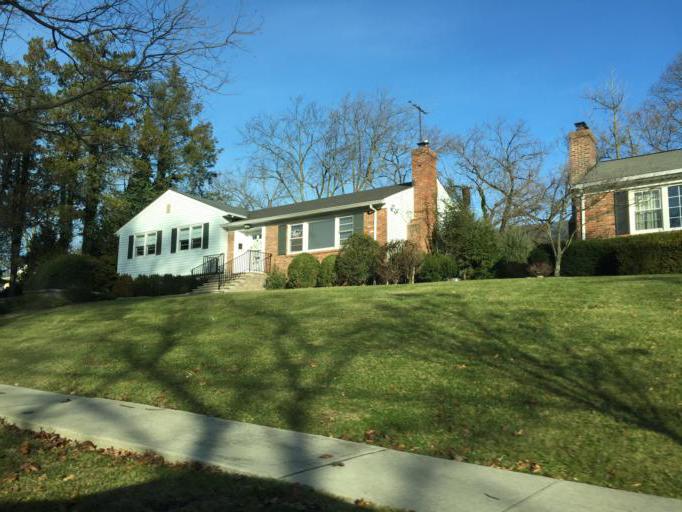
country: US
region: New Jersey
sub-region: Union County
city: Summit
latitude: 40.7162
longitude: -74.3704
